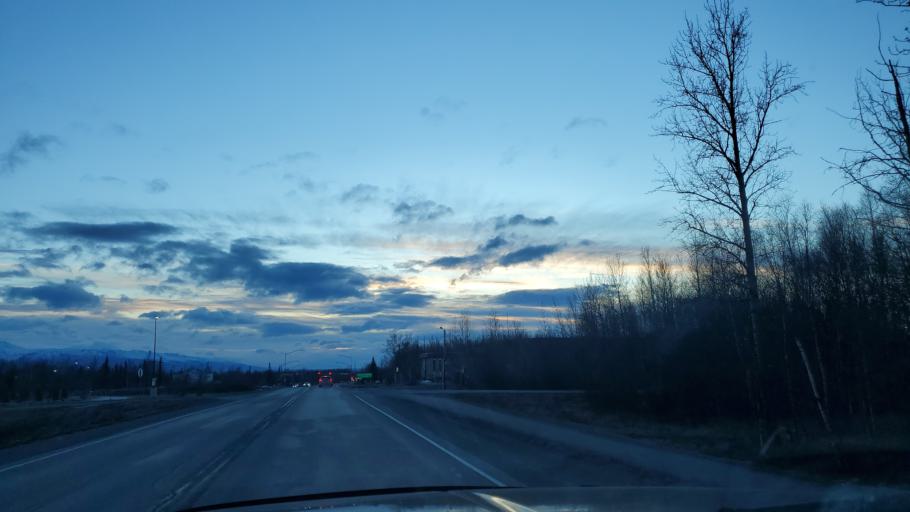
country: US
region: Alaska
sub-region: Matanuska-Susitna Borough
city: Wasilla
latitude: 61.5736
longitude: -149.4425
